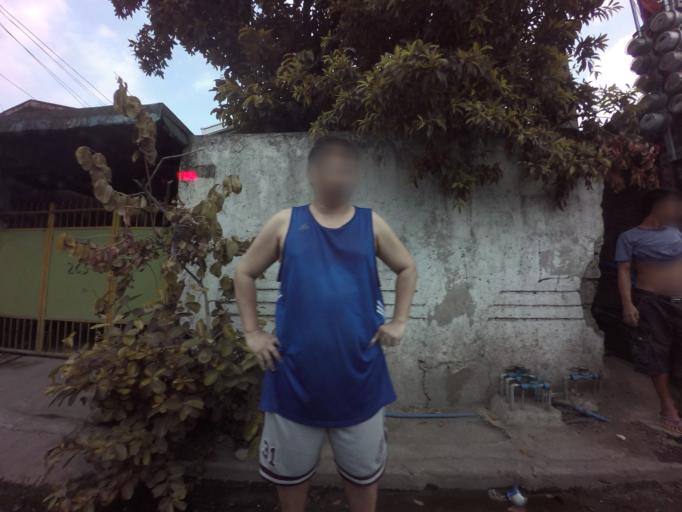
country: PH
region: Calabarzon
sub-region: Province of Rizal
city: Taguig
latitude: 14.4769
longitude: 121.0603
